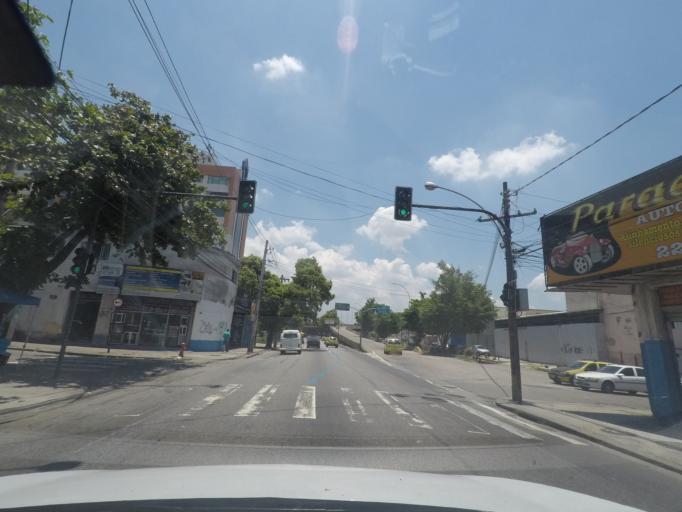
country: BR
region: Rio de Janeiro
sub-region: Rio De Janeiro
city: Rio de Janeiro
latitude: -22.9024
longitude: -43.2580
